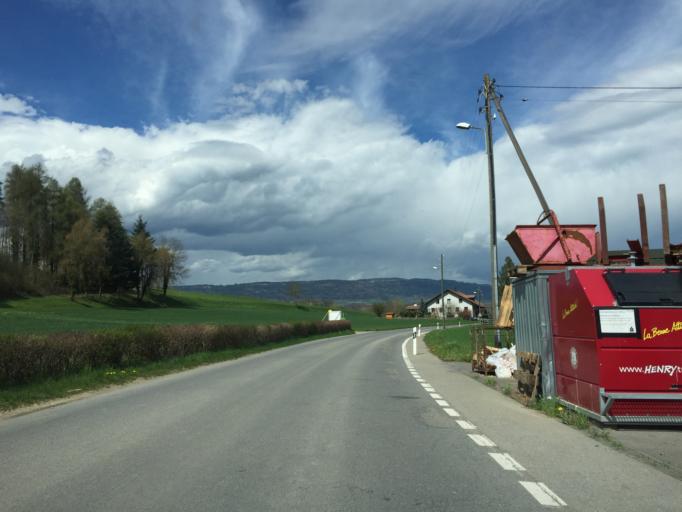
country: CH
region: Vaud
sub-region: Morges District
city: Grancy
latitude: 46.5942
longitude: 6.4616
